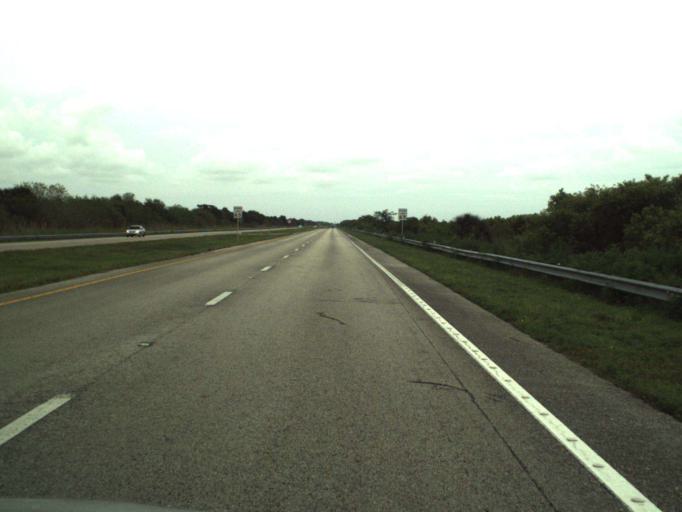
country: US
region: Florida
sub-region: Orange County
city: Christmas
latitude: 28.5436
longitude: -80.9278
